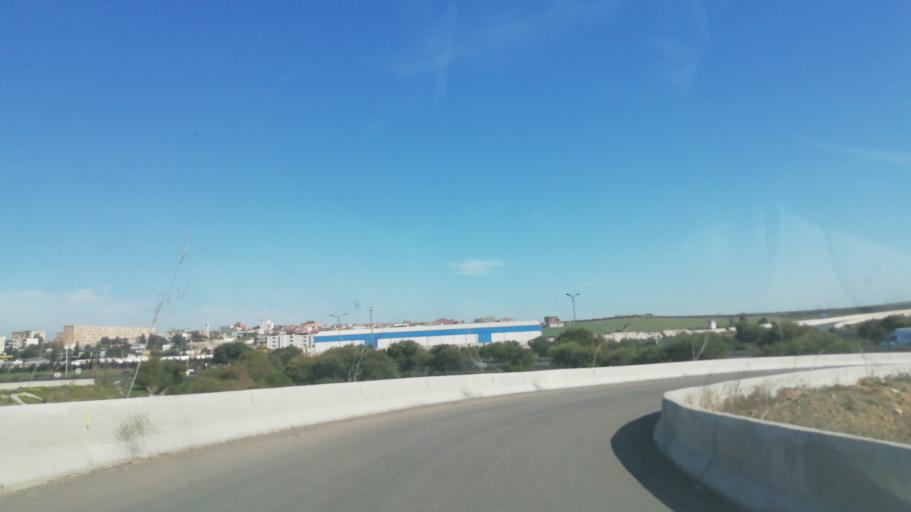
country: DZ
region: Oran
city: Es Senia
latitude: 35.6021
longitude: -0.5757
